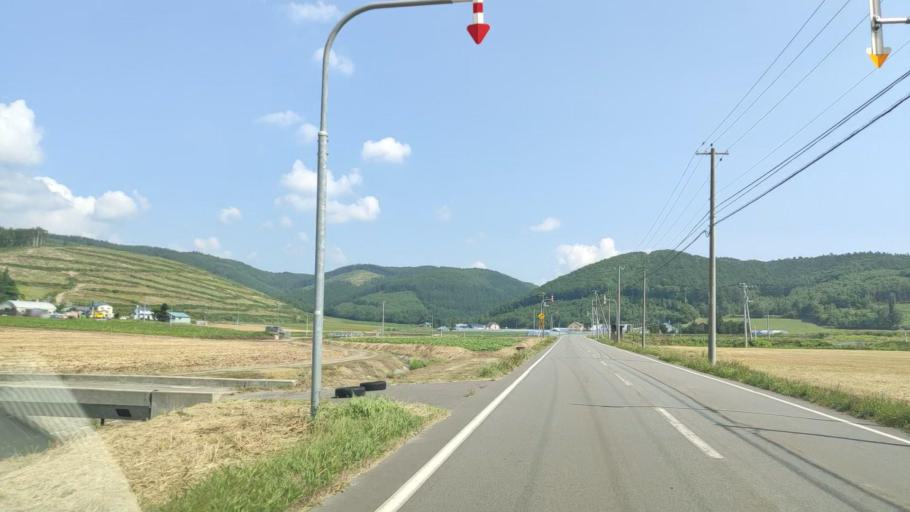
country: JP
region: Hokkaido
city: Shimo-furano
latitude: 43.4142
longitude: 142.3992
